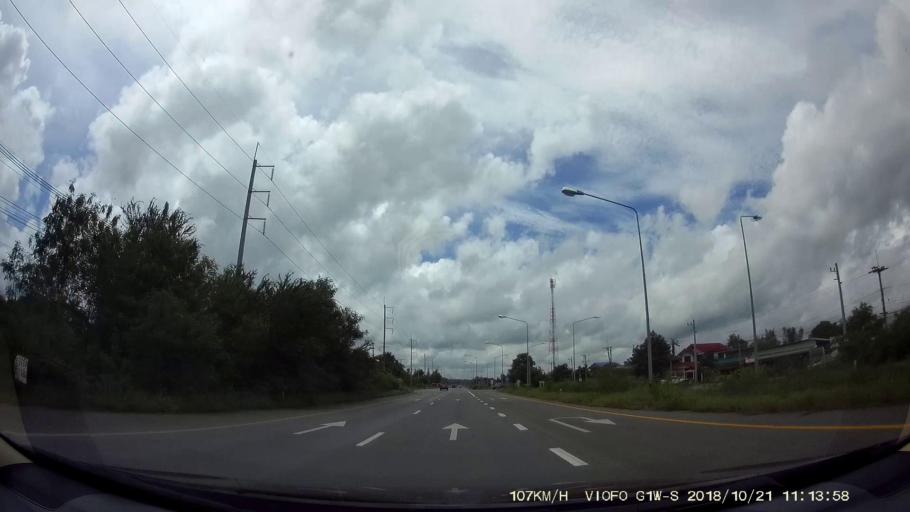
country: TH
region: Chaiyaphum
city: Chaiyaphum
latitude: 15.9098
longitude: 102.1272
